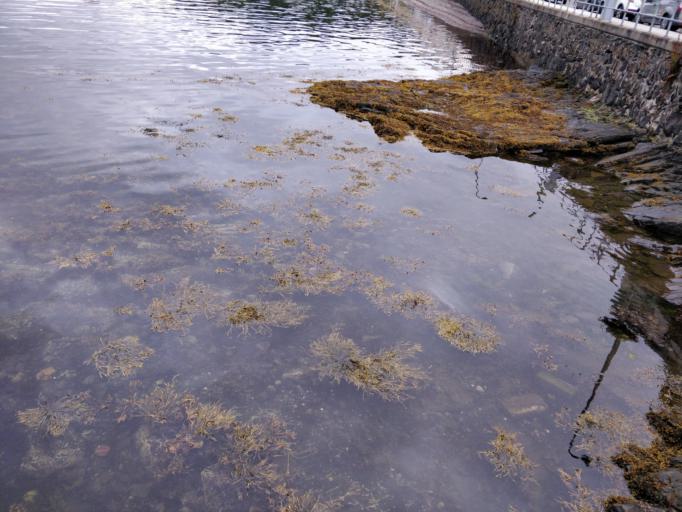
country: GB
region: Scotland
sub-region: Argyll and Bute
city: Oban
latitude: 56.4158
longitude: -5.4741
